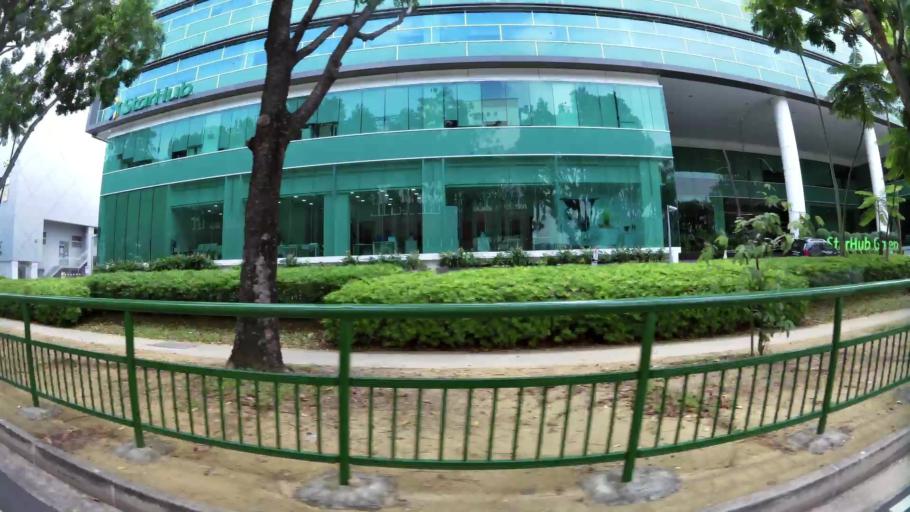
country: SG
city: Singapore
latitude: 1.3247
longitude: 103.8928
